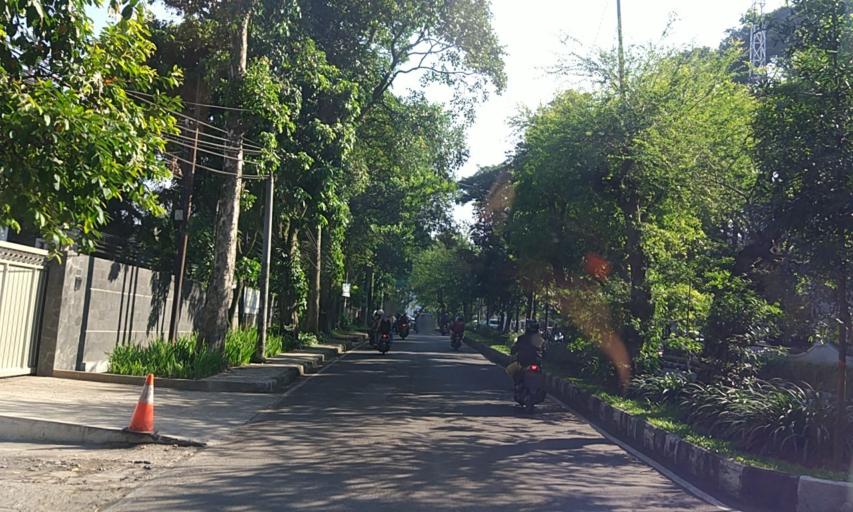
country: ID
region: West Java
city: Bandung
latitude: -6.9029
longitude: 107.6169
